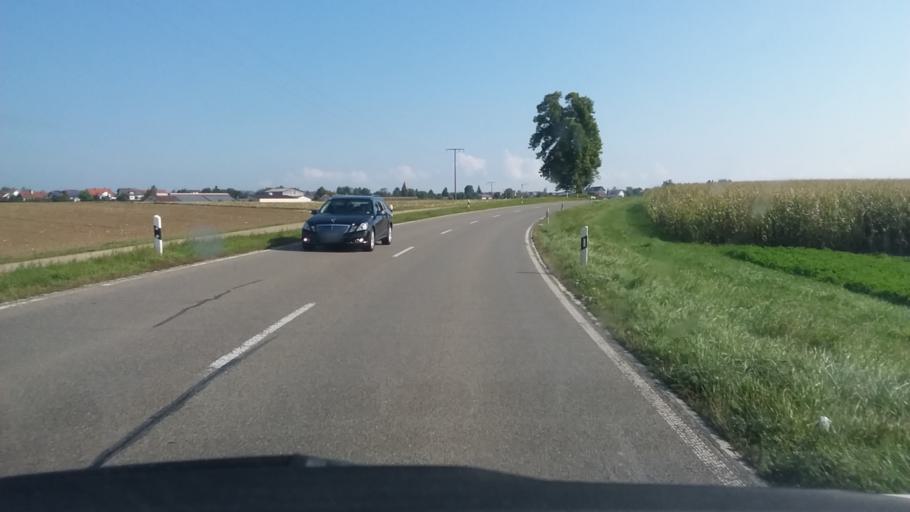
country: DE
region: Baden-Wuerttemberg
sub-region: Tuebingen Region
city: Nellingen
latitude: 48.5345
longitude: 9.7822
